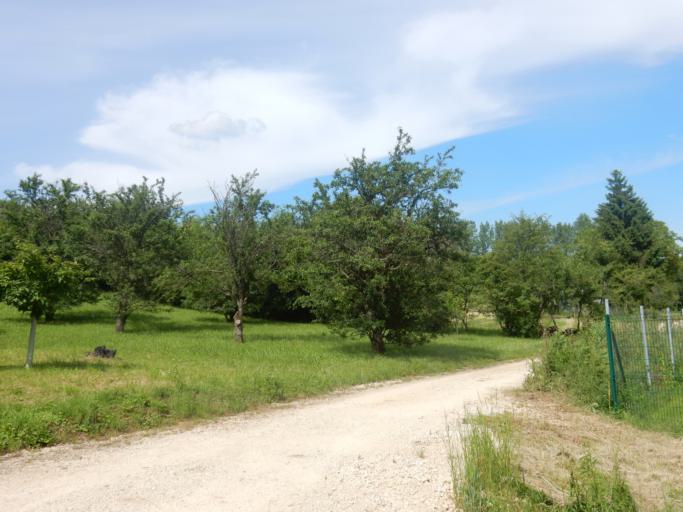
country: FR
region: Lorraine
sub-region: Departement de Meurthe-et-Moselle
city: Pagny-sur-Moselle
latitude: 48.9741
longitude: 5.9985
